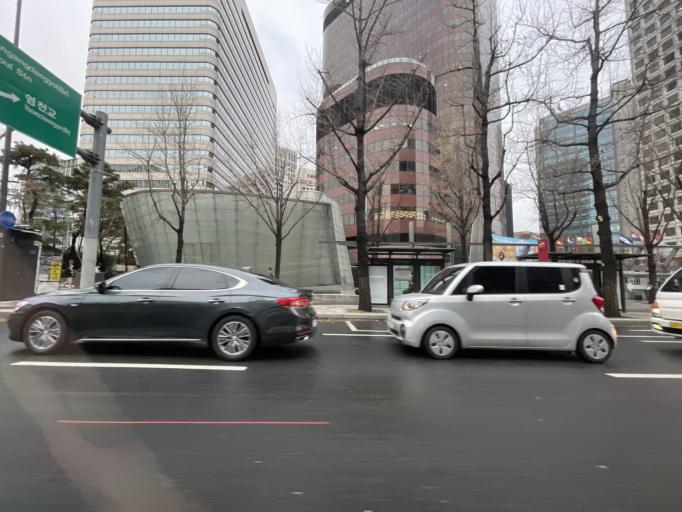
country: KR
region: Seoul
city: Seoul
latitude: 37.5613
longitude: 126.9758
